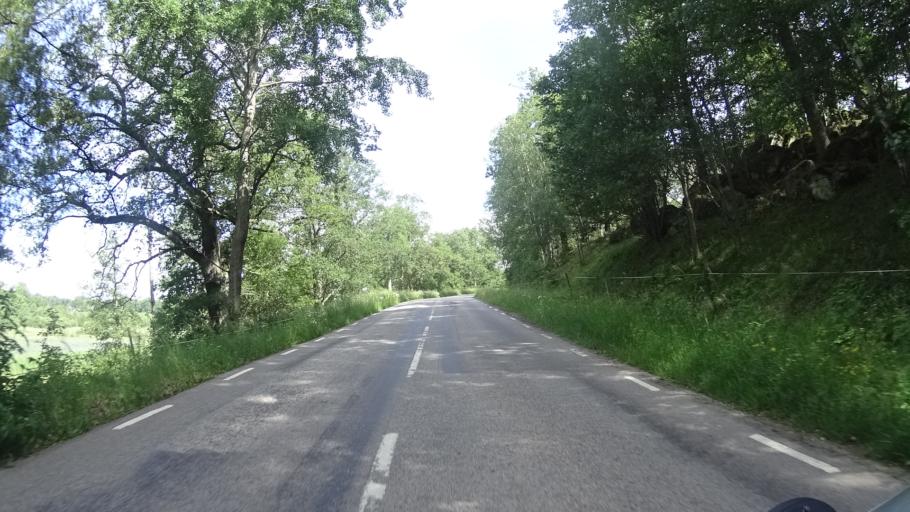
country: SE
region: Kalmar
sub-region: Vasterviks Kommun
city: Overum
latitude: 57.9003
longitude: 16.1726
